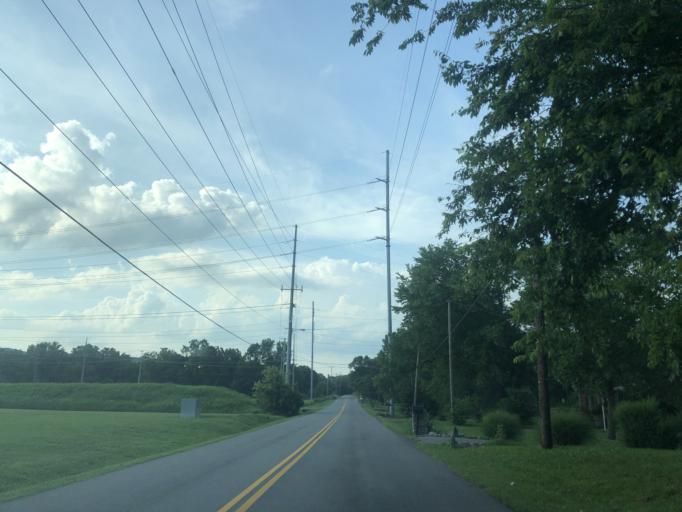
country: US
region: Tennessee
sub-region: Davidson County
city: Nashville
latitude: 36.2452
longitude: -86.8289
